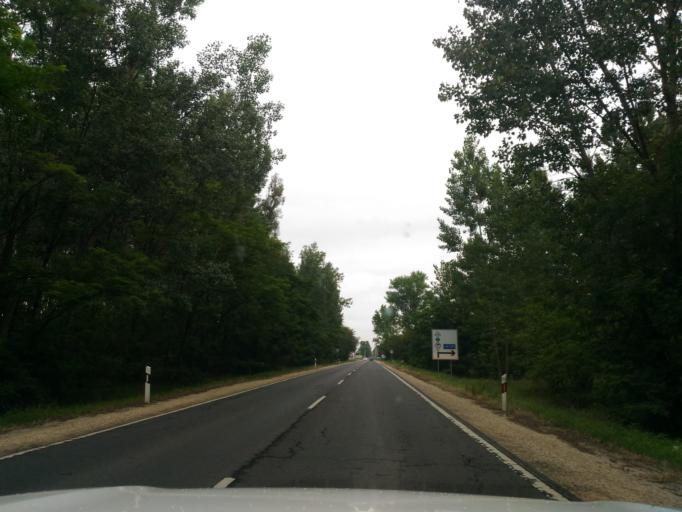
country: HU
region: Pest
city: Alsonemedi
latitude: 47.2980
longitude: 19.1827
